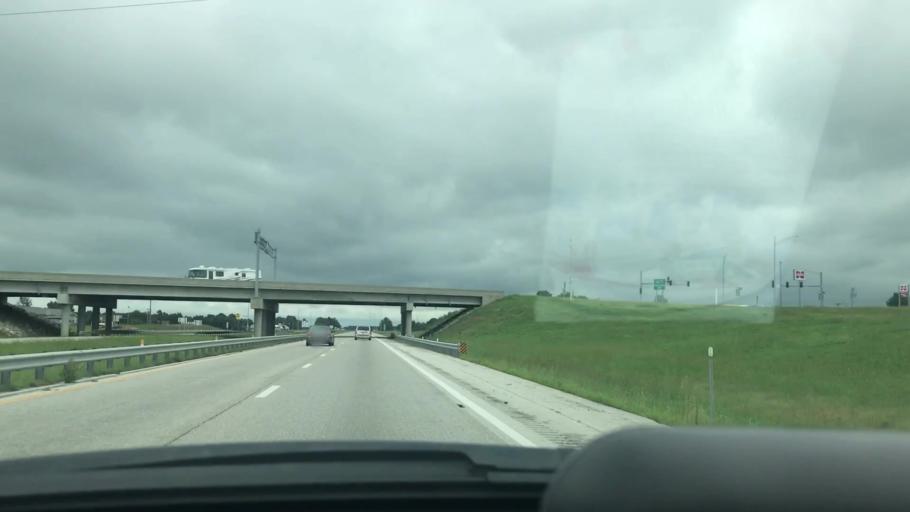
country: US
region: Missouri
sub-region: Lawrence County
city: Mount Vernon
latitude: 37.0927
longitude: -93.8048
